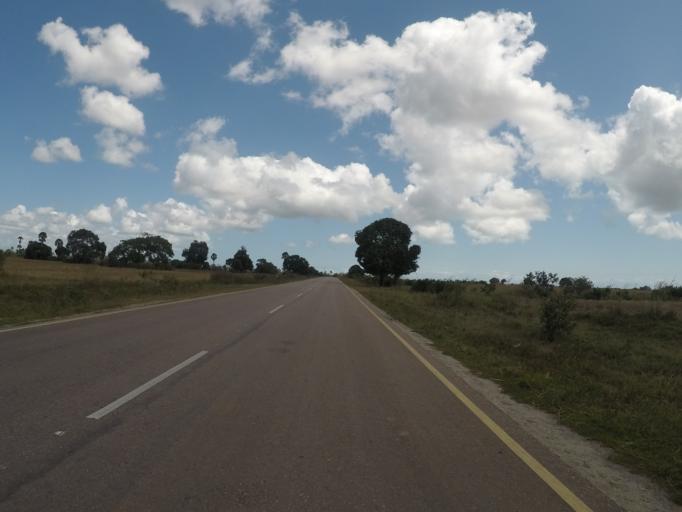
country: TZ
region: Zanzibar Central/South
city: Koani
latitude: -6.1942
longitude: 39.3705
